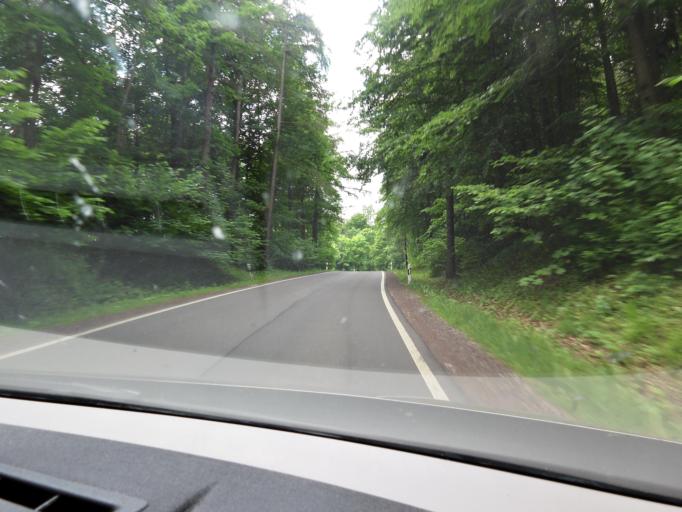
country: DE
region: Thuringia
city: Ernstroda
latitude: 50.8542
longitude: 10.6188
